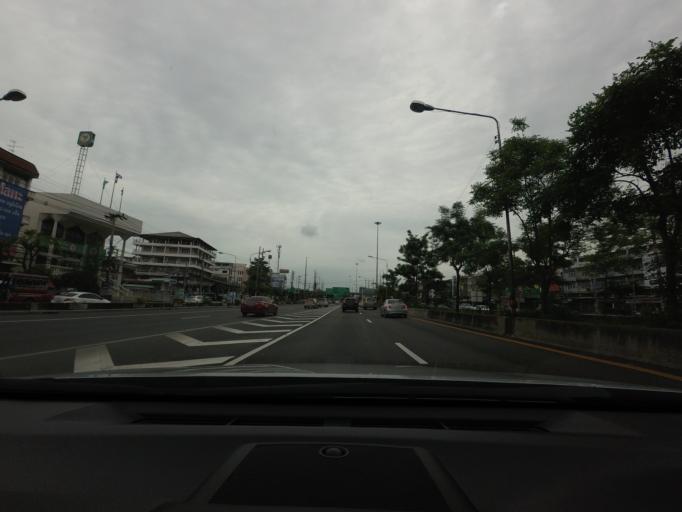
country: TH
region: Bangkok
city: Chom Thong
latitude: 13.6807
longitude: 100.4739
